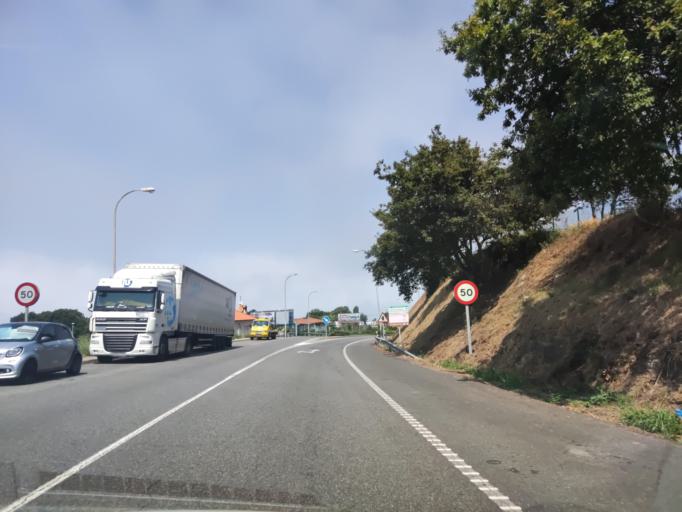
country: ES
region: Galicia
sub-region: Provincia de Pontevedra
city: Redondela
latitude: 42.2738
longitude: -8.6659
